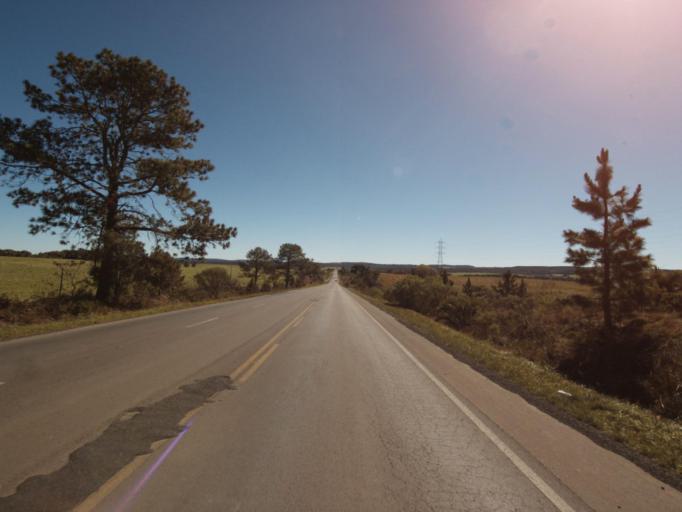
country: BR
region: Santa Catarina
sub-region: Concordia
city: Concordia
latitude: -26.9470
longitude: -51.8605
